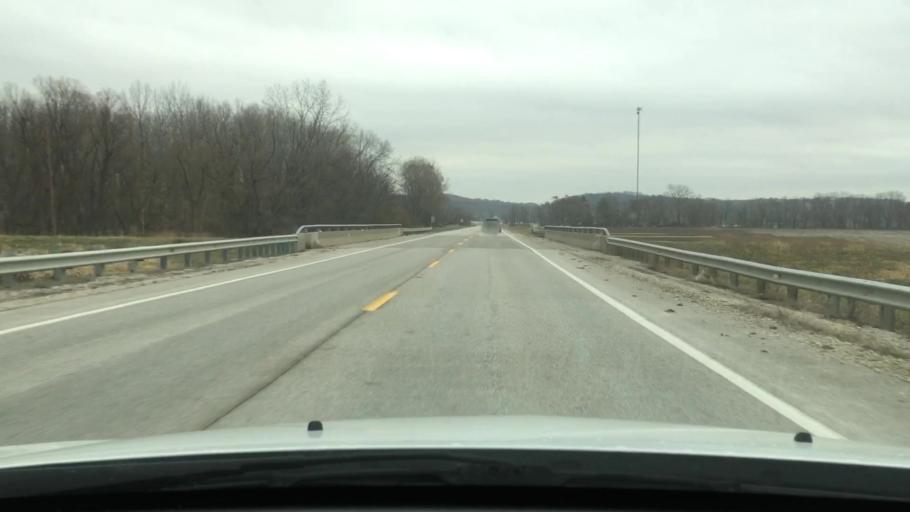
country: US
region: Missouri
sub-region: Pike County
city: Louisiana
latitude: 39.5037
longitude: -90.9895
